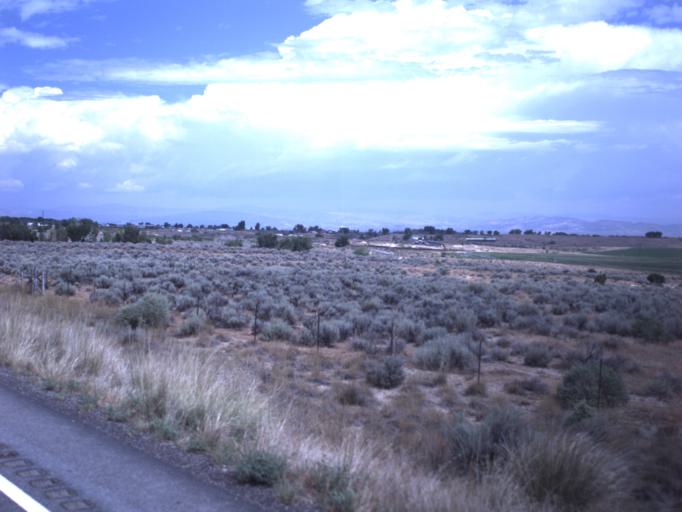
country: US
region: Utah
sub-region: Uintah County
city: Naples
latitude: 40.3524
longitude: -109.4934
